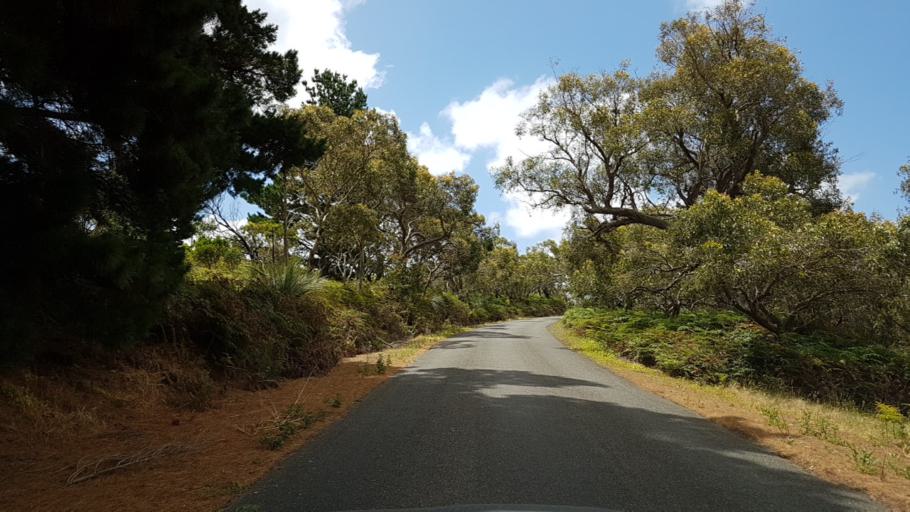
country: AU
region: South Australia
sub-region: Victor Harbor
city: Victor Harbor
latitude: -35.4553
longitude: 138.5928
